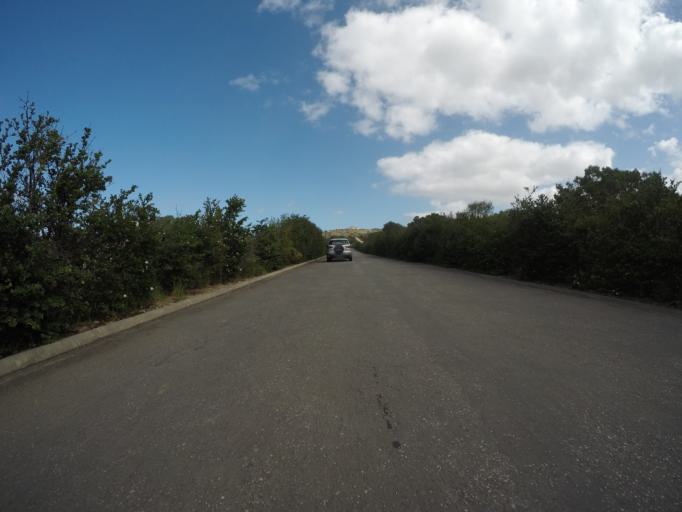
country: ZA
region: Western Cape
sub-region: Eden District Municipality
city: Mossel Bay
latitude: -34.1433
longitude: 22.0887
